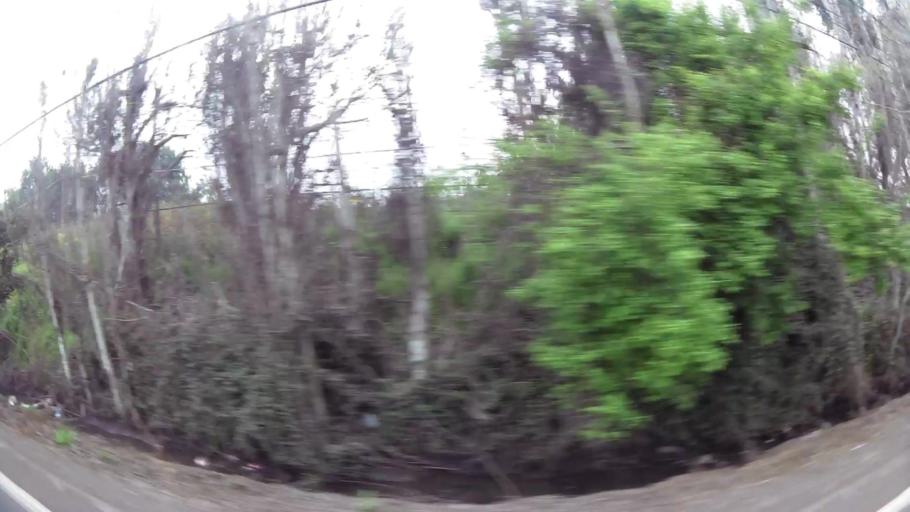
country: CL
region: Santiago Metropolitan
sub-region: Provincia de Chacabuco
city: Chicureo Abajo
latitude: -33.2579
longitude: -70.7625
